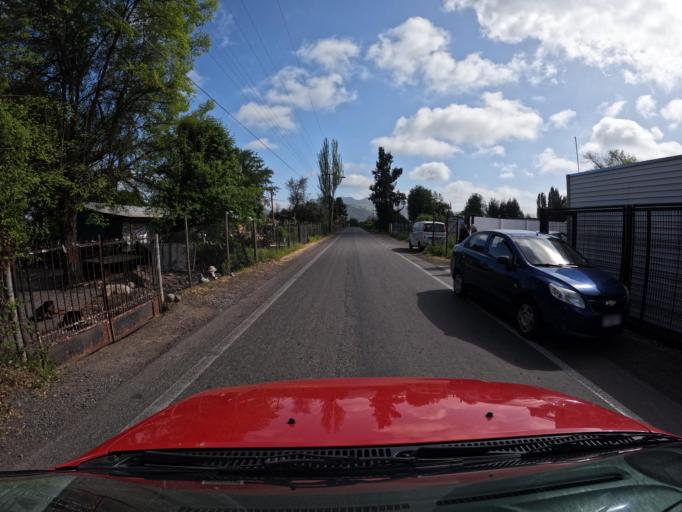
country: CL
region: Maule
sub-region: Provincia de Curico
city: Teno
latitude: -34.8743
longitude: -71.2257
